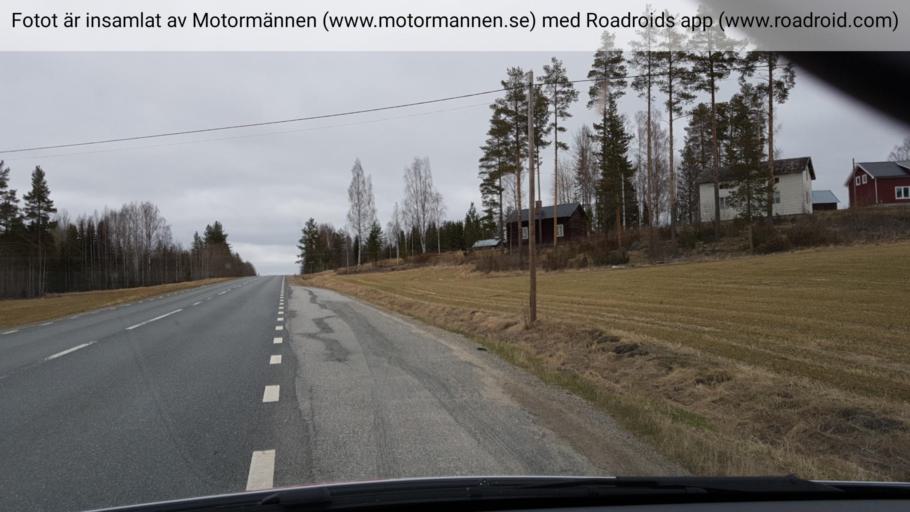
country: SE
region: Vaesternorrland
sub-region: OErnskoeldsviks Kommun
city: Ornskoldsvik
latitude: 63.5764
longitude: 18.5496
